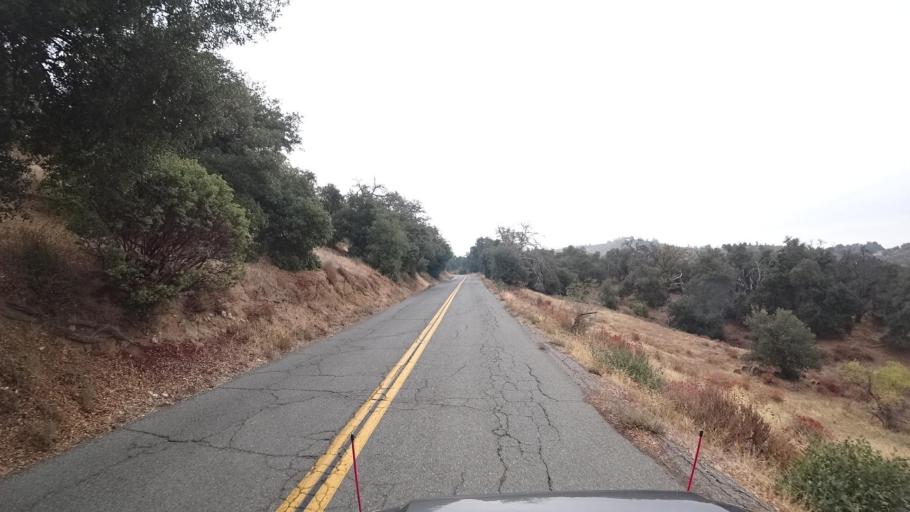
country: US
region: California
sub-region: San Diego County
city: Julian
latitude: 33.0632
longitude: -116.6114
